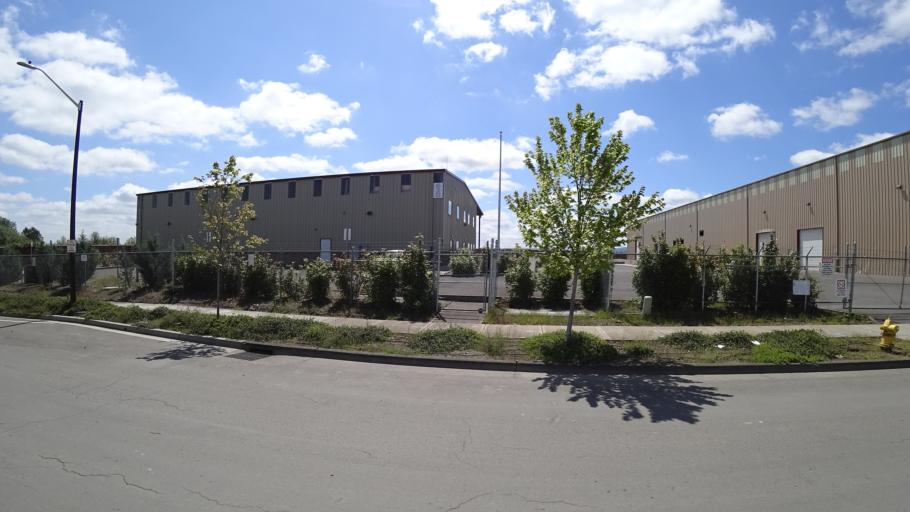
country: US
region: Oregon
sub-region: Washington County
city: Hillsboro
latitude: 45.5126
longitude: -122.9962
